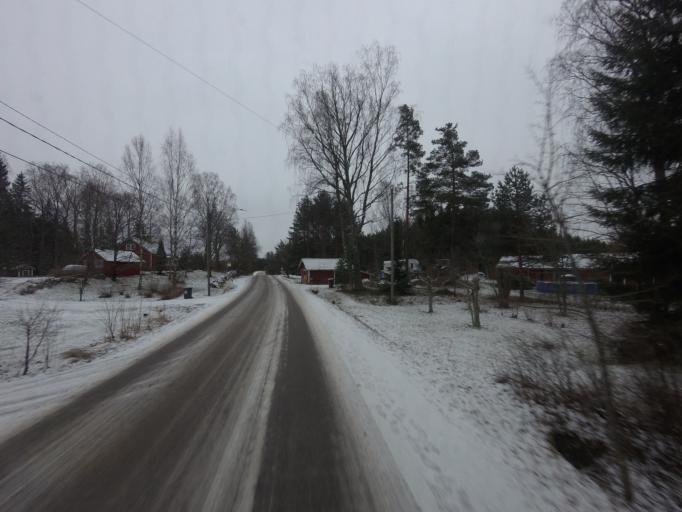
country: FI
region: Uusimaa
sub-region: Helsinki
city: Espoo
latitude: 60.1984
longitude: 24.5603
